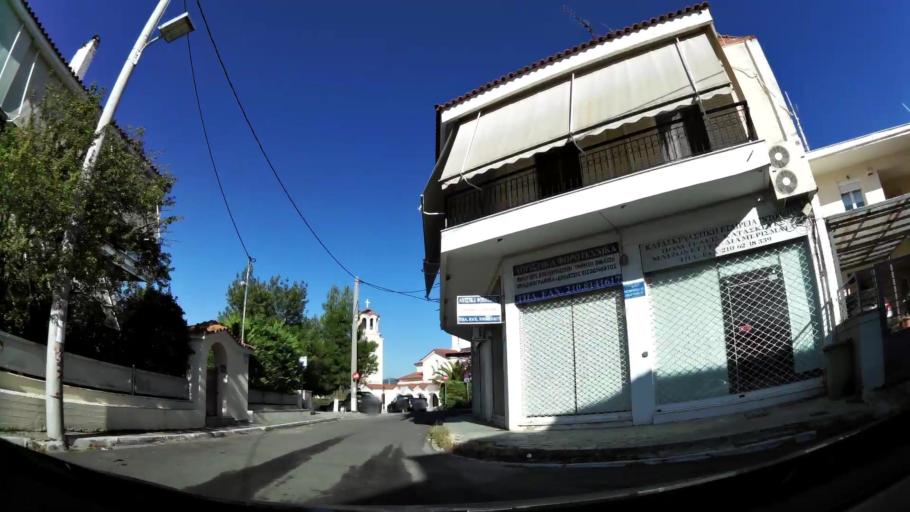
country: GR
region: Attica
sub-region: Nomarchia Anatolikis Attikis
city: Anoixi
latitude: 38.1326
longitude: 23.8608
